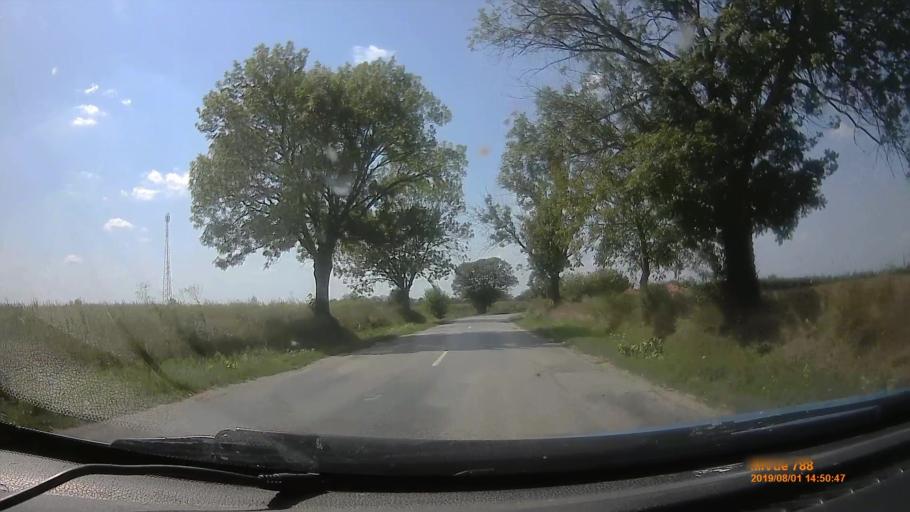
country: HU
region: Baranya
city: Vajszlo
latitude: 45.8533
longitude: 18.0010
